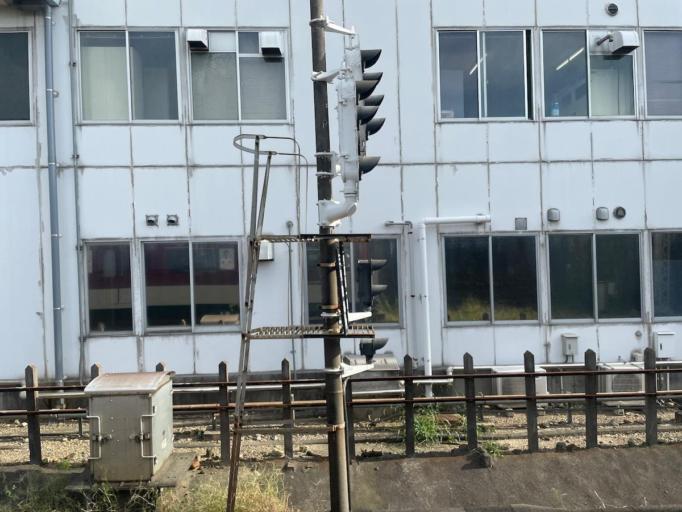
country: JP
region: Aichi
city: Nagoya-shi
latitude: 35.1596
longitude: 136.8763
